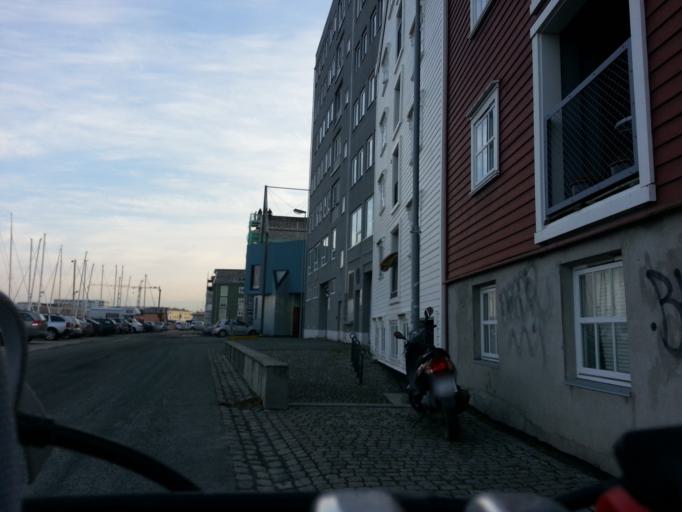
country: NO
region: Sor-Trondelag
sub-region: Trondheim
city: Trondheim
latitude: 63.4329
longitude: 10.3891
